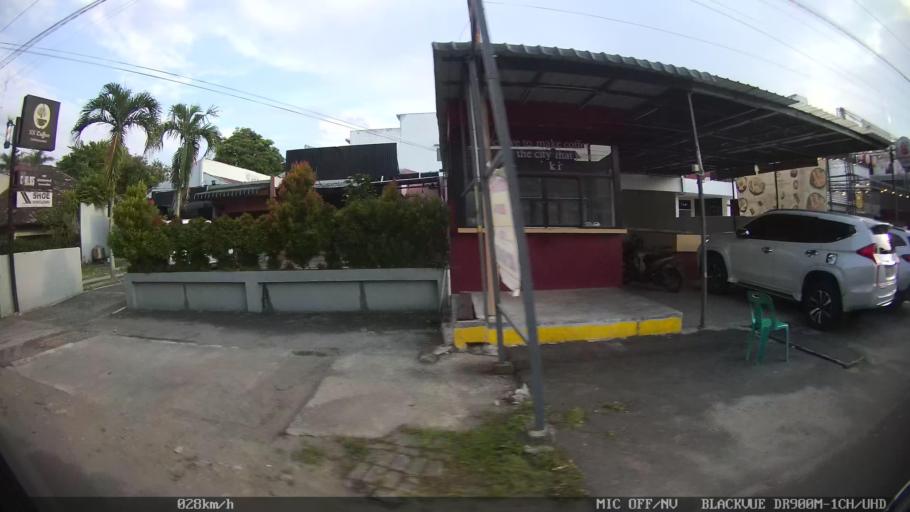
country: ID
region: North Sumatra
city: Medan
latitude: 3.5766
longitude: 98.6636
